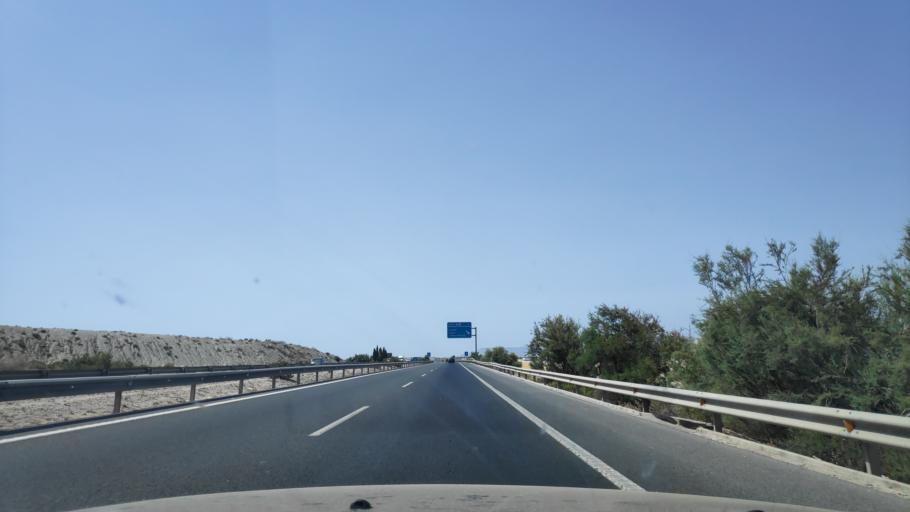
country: ES
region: Murcia
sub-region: Murcia
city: Lorqui
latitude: 38.0916
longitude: -1.2256
